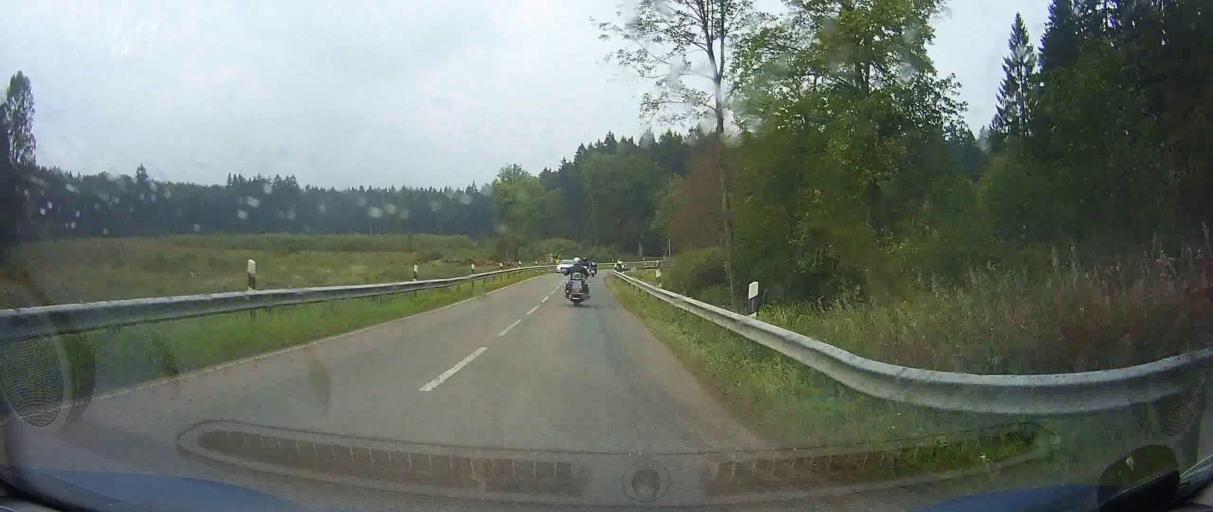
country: DE
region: Lower Saxony
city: Uslar
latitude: 51.7198
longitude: 9.6150
